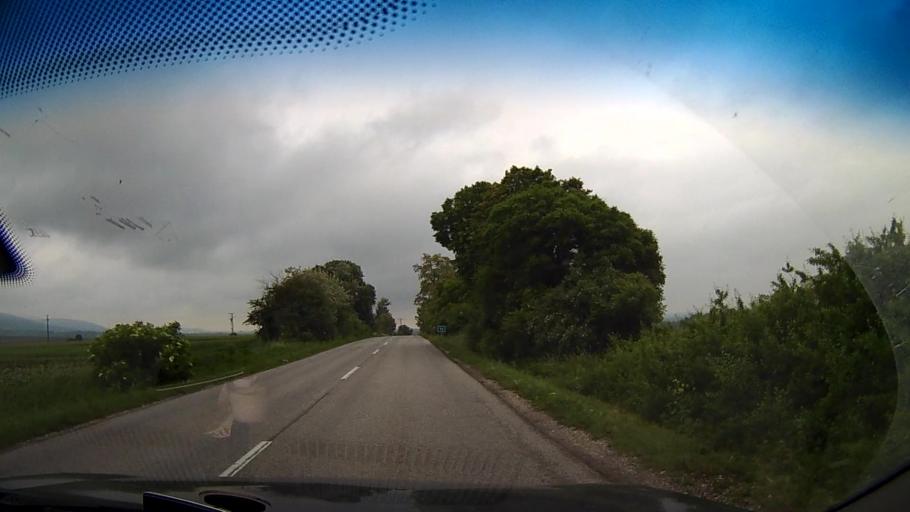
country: HU
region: Pest
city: Perbal
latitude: 47.5977
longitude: 18.7706
